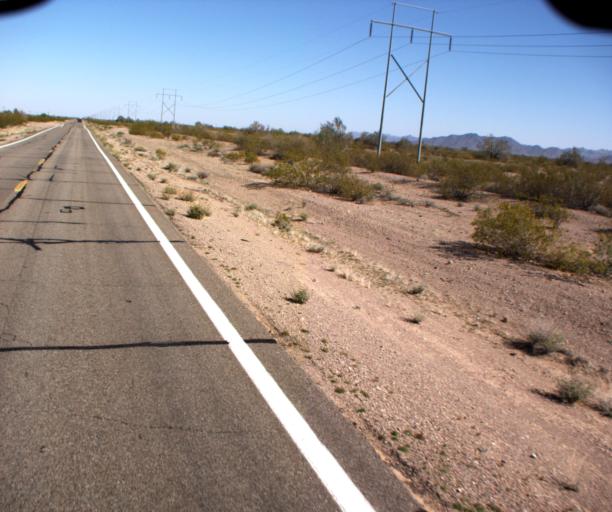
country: US
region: Arizona
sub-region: La Paz County
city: Quartzsite
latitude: 33.4853
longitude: -114.2170
